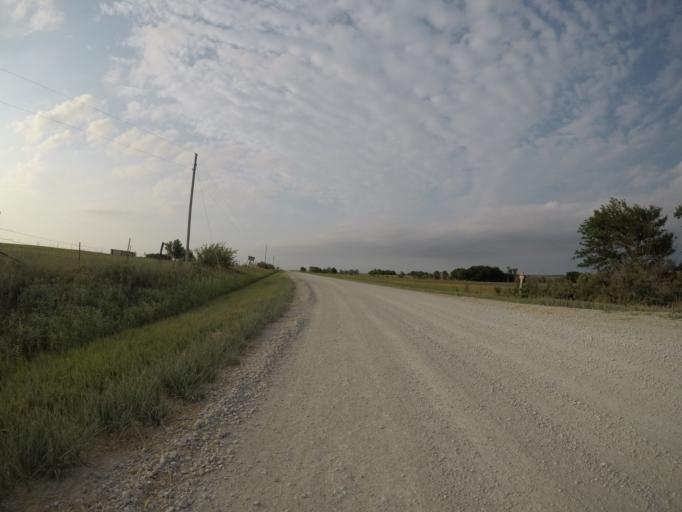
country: US
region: Kansas
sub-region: Wabaunsee County
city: Alma
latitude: 39.1023
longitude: -96.3456
